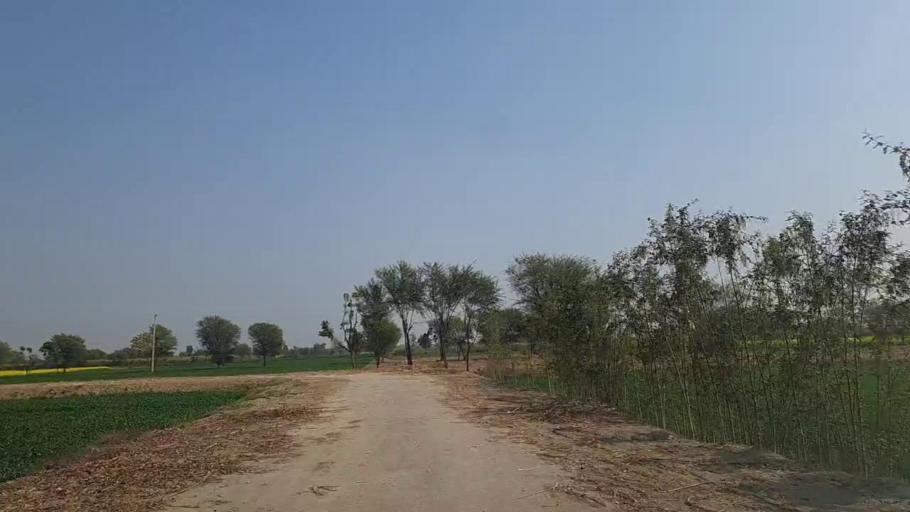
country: PK
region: Sindh
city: Daur
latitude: 26.4929
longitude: 68.4484
